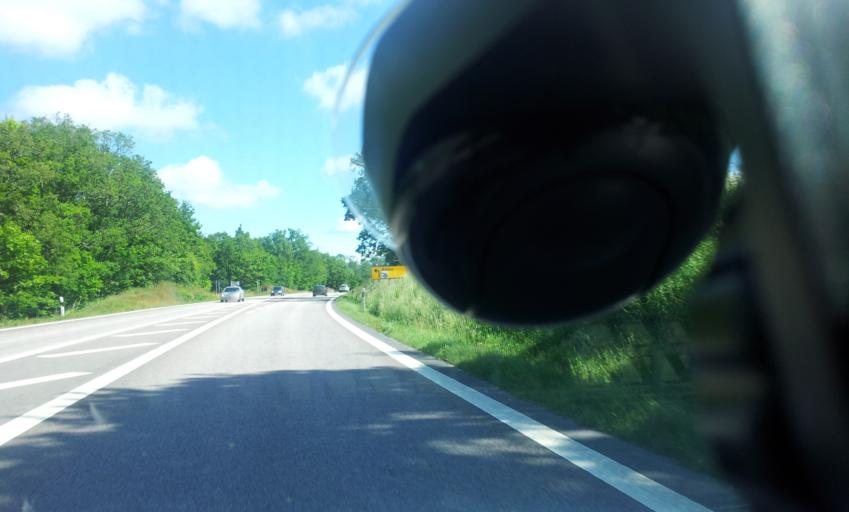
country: SE
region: Kalmar
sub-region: Monsteras Kommun
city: Moensteras
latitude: 57.0562
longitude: 16.4404
